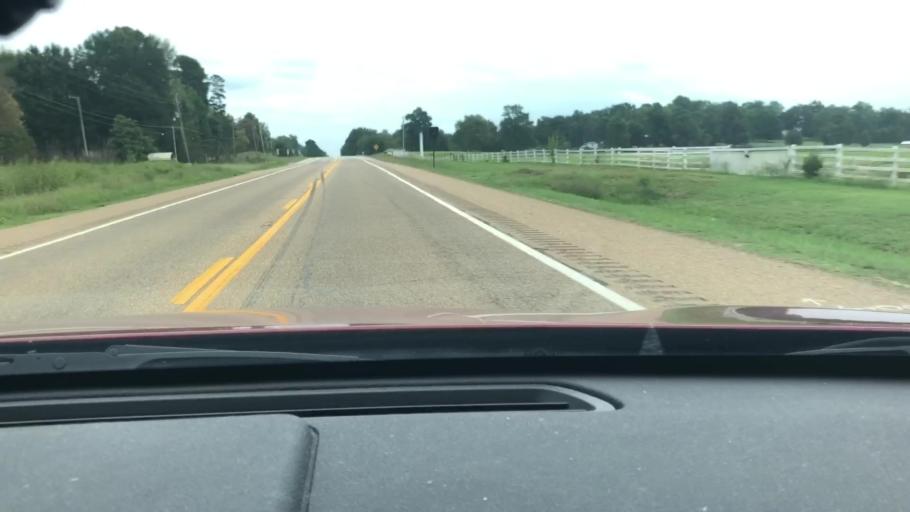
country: US
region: Arkansas
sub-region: Miller County
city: Texarkana
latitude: 33.4292
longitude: -93.9310
